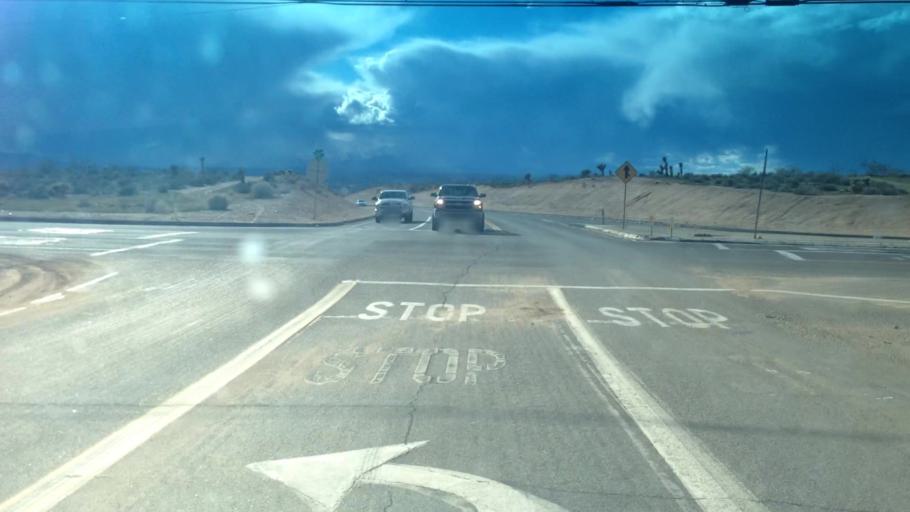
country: US
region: California
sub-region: San Bernardino County
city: Apple Valley
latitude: 34.4207
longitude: -117.2070
